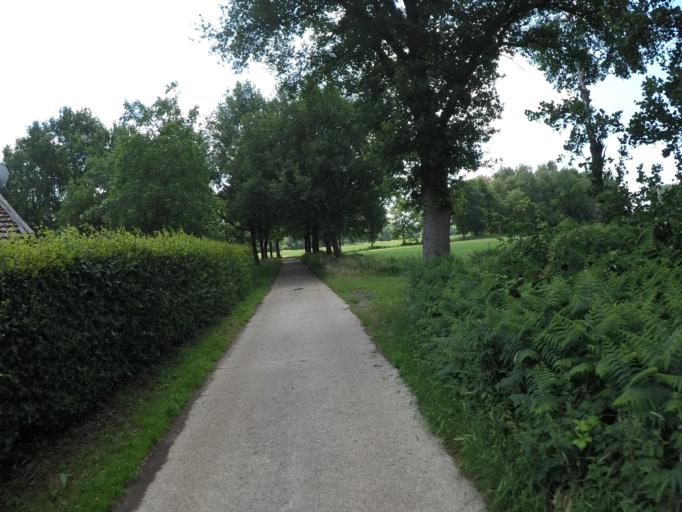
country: BE
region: Flanders
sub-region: Provincie Antwerpen
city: Vosselaar
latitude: 51.2734
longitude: 4.8906
